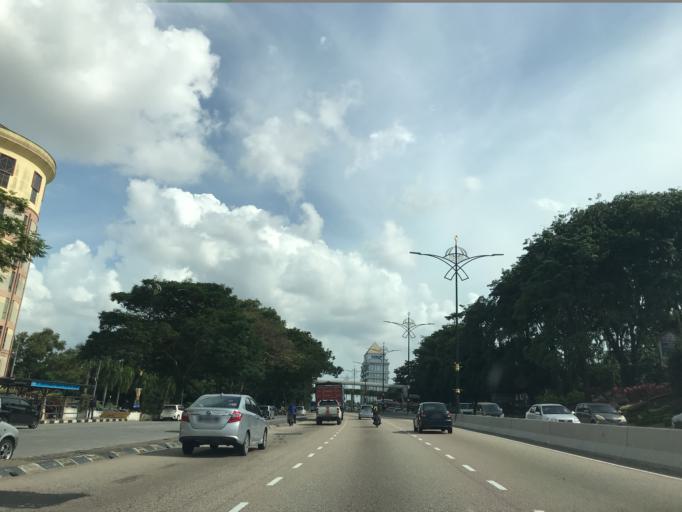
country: MY
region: Johor
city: Skudai
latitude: 1.5413
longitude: 103.6593
